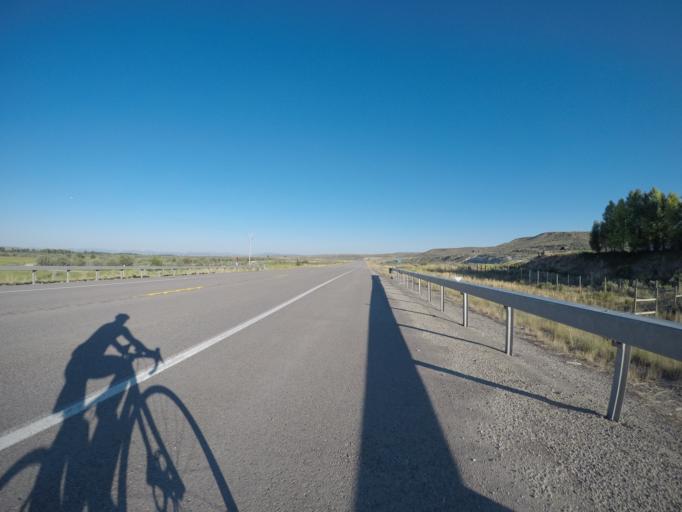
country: US
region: Wyoming
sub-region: Sublette County
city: Pinedale
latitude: 42.8830
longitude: -109.9992
